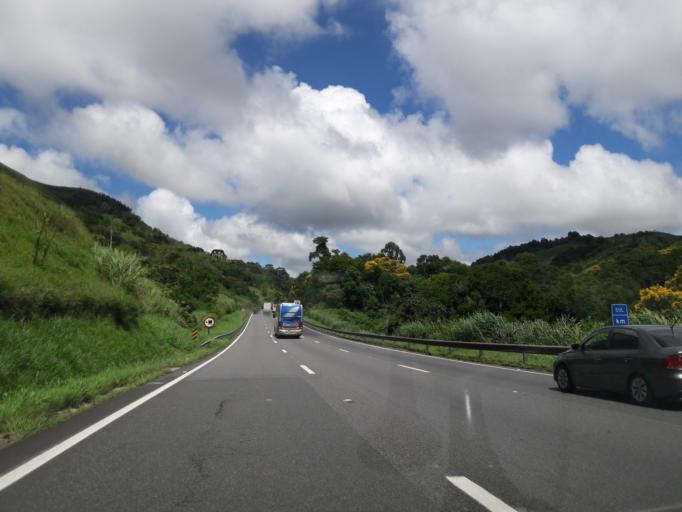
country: BR
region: Sao Paulo
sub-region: Cajati
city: Cajati
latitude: -24.9625
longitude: -48.4779
